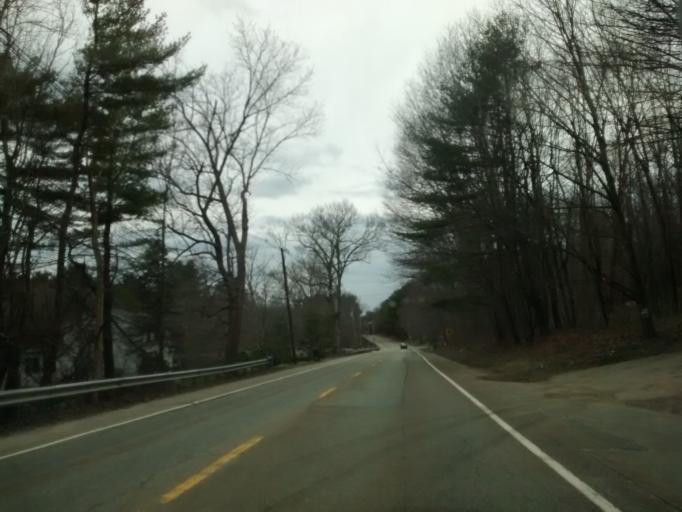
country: US
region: Massachusetts
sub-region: Worcester County
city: Charlton
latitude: 42.1281
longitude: -72.0050
